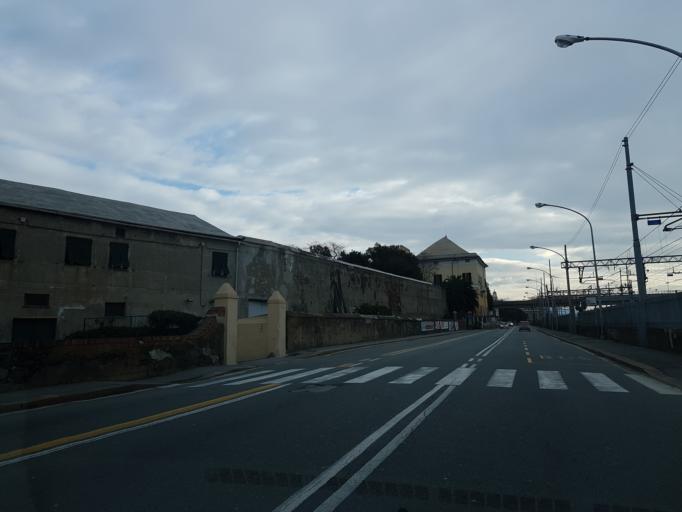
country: IT
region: Liguria
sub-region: Provincia di Genova
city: Mele
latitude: 44.4281
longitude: 8.7666
